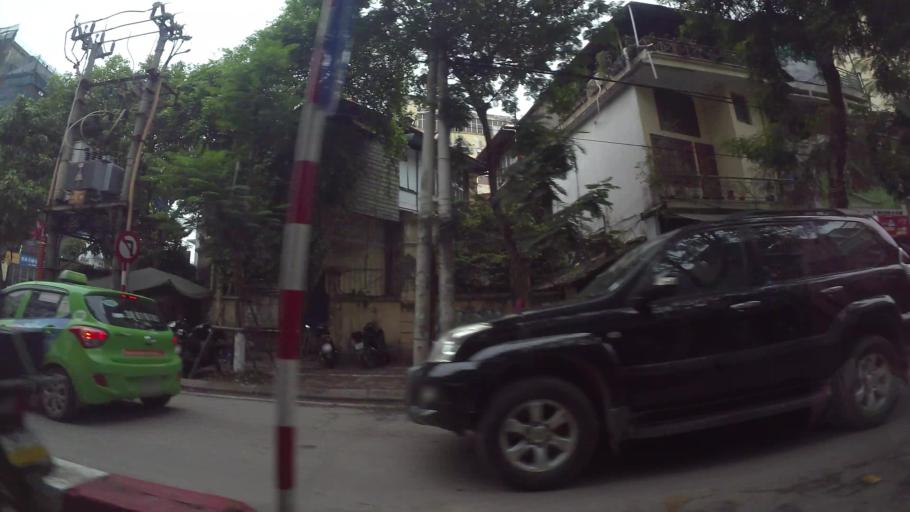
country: VN
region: Ha Noi
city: Hai BaTrung
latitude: 21.0195
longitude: 105.8522
